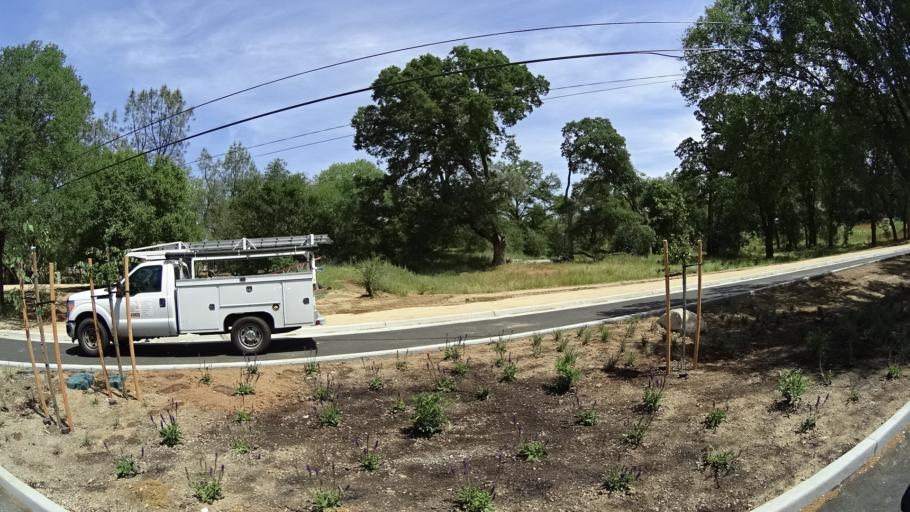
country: US
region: California
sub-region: Placer County
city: Rocklin
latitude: 38.7827
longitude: -121.2383
